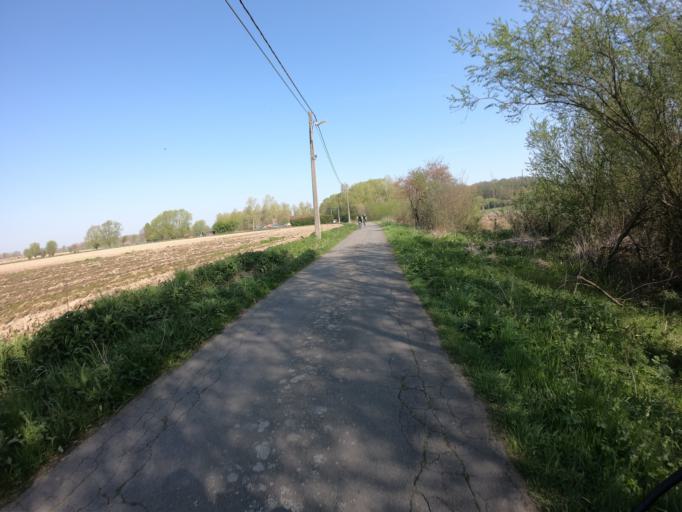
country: BE
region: Wallonia
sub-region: Province du Hainaut
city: Lessines
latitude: 50.7385
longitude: 3.8578
